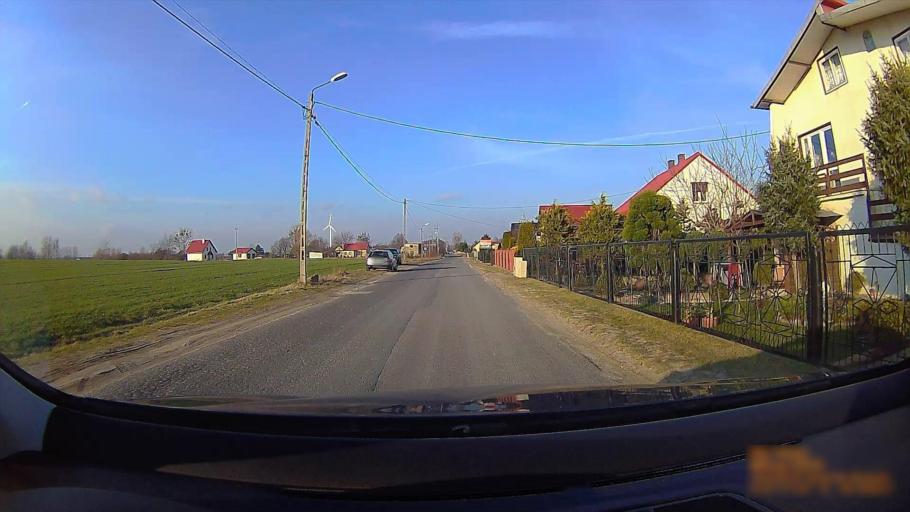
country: PL
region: Greater Poland Voivodeship
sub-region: Konin
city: Konin
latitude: 52.1858
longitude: 18.3318
